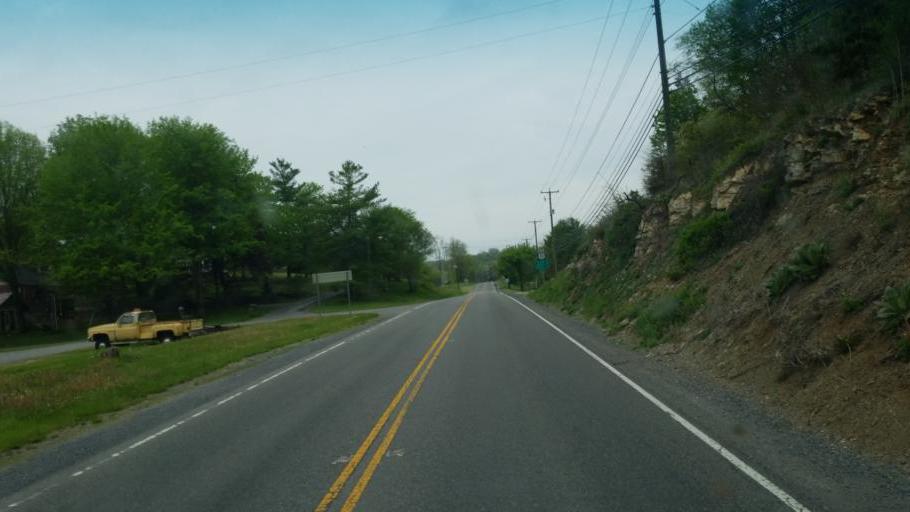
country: US
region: Virginia
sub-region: Smyth County
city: Marion
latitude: 36.8204
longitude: -81.5507
